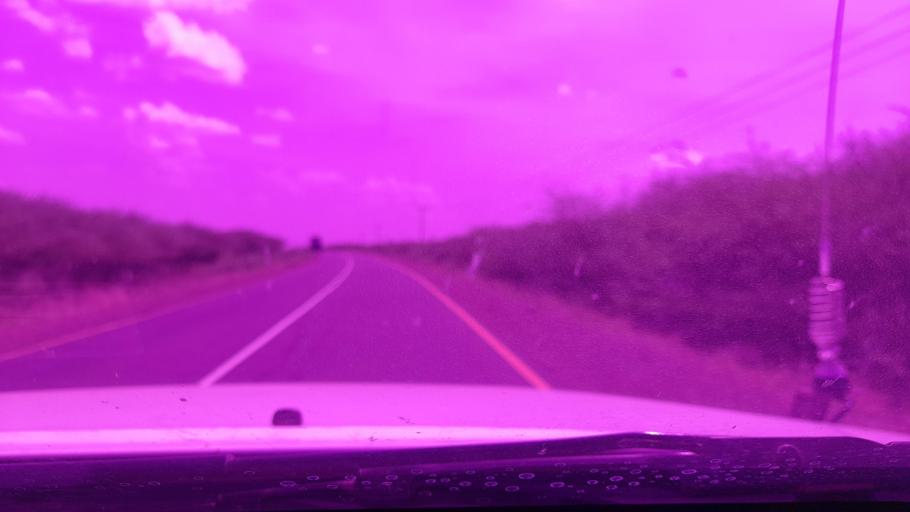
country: ET
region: Afar
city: Awash
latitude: 9.3549
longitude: 40.3033
